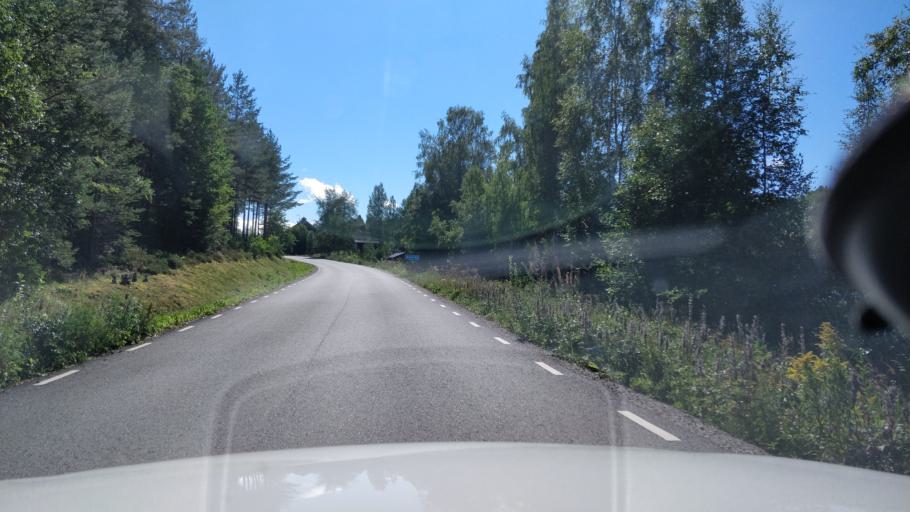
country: SE
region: Dalarna
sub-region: Faluns Kommun
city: Bjursas
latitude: 60.7479
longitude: 15.4727
